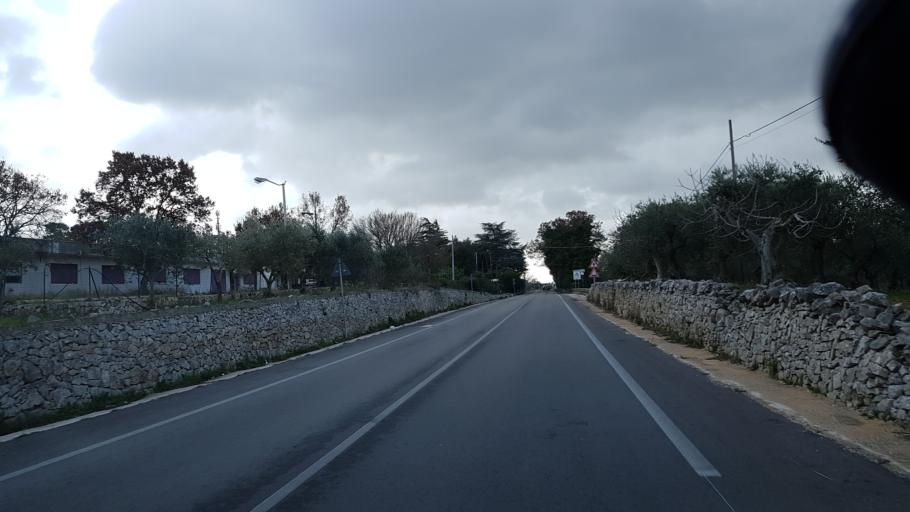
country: IT
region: Apulia
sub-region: Provincia di Bari
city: Locorotondo
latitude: 40.7798
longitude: 17.3383
